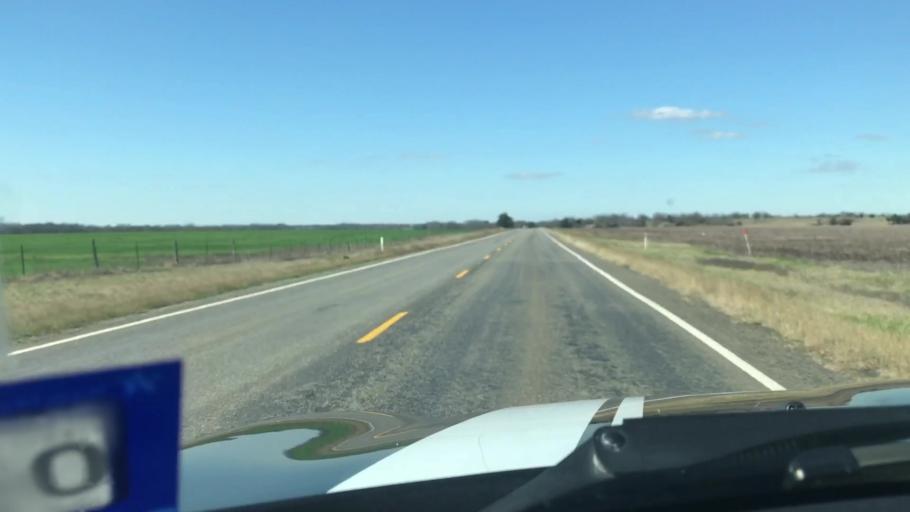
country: US
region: Texas
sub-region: Robertson County
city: Calvert
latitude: 30.8733
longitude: -96.7196
